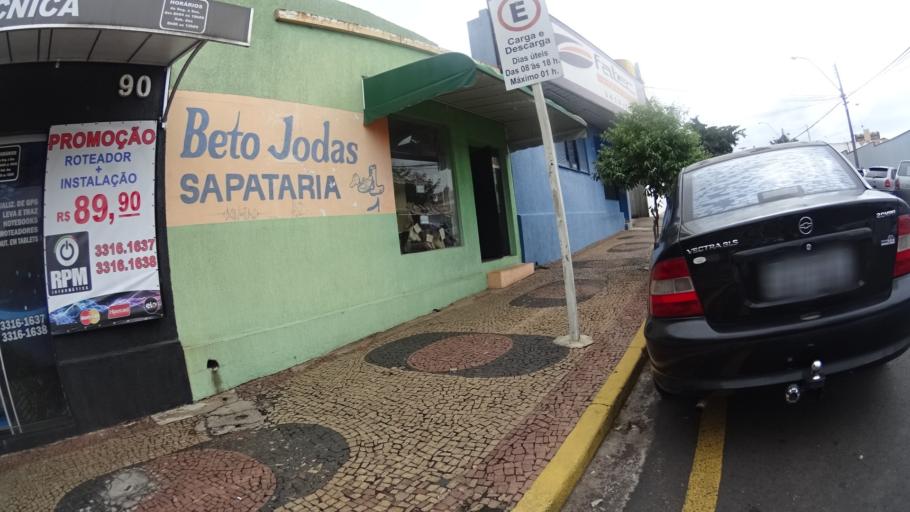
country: BR
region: Sao Paulo
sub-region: Marilia
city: Marilia
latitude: -22.2182
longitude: -49.9426
